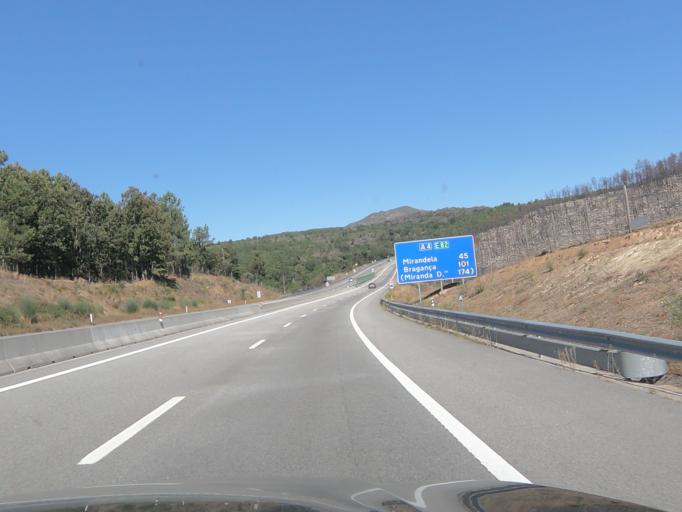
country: PT
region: Vila Real
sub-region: Sabrosa
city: Sabrosa
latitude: 41.3549
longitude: -7.5973
